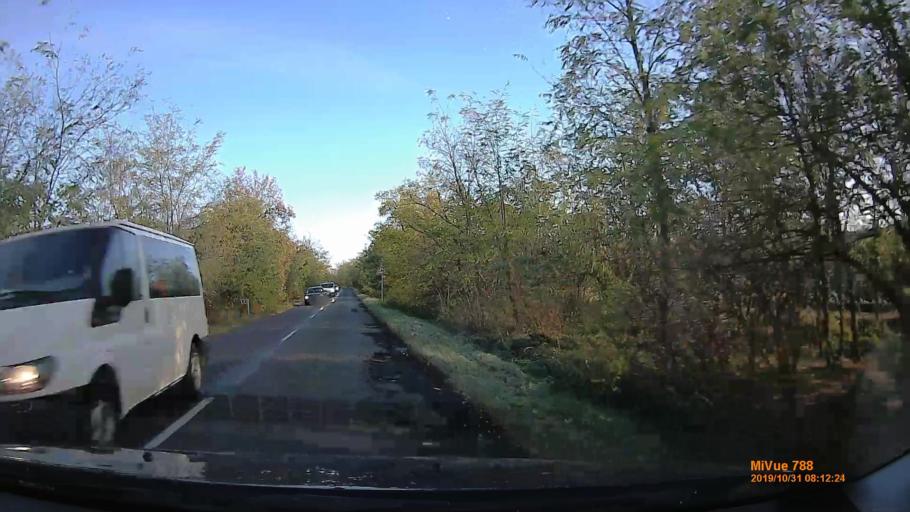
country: HU
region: Pest
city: Pilis
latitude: 47.3246
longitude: 19.5667
